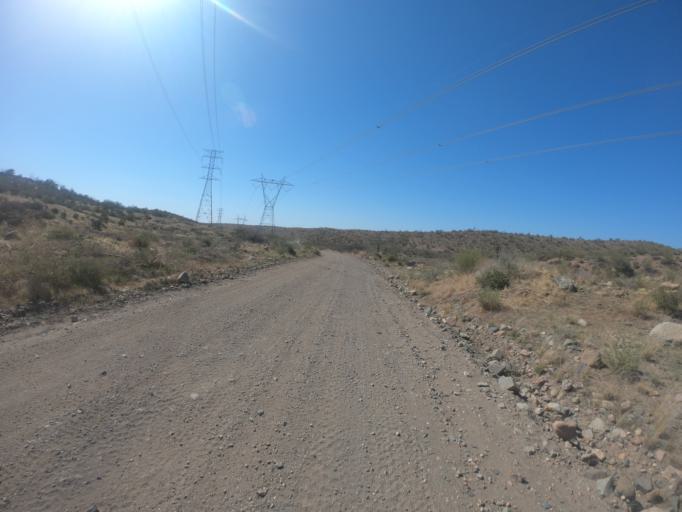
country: US
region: Arizona
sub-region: Pinal County
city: Superior
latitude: 33.2979
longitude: -111.1373
